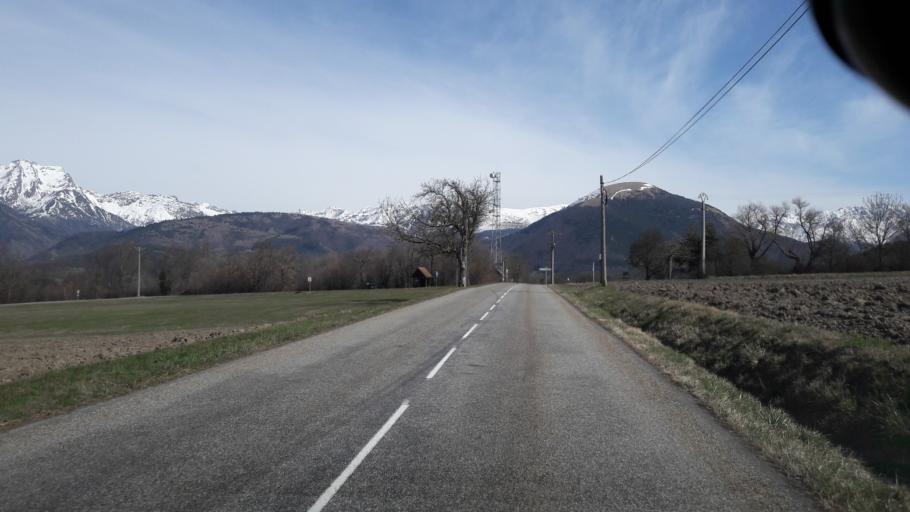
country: FR
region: Rhone-Alpes
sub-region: Departement de l'Isere
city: La Mure
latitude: 44.8441
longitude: 5.8101
